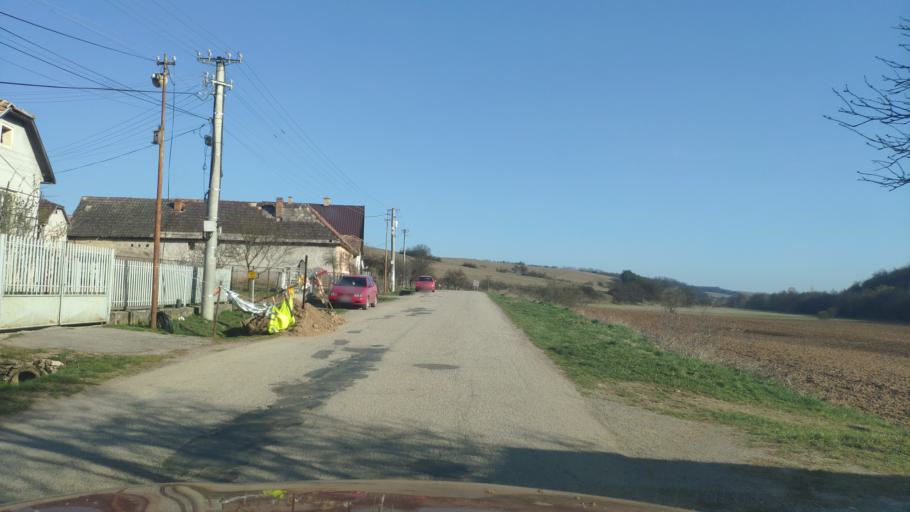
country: SK
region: Banskobystricky
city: Revuca
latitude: 48.5388
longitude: 20.2412
